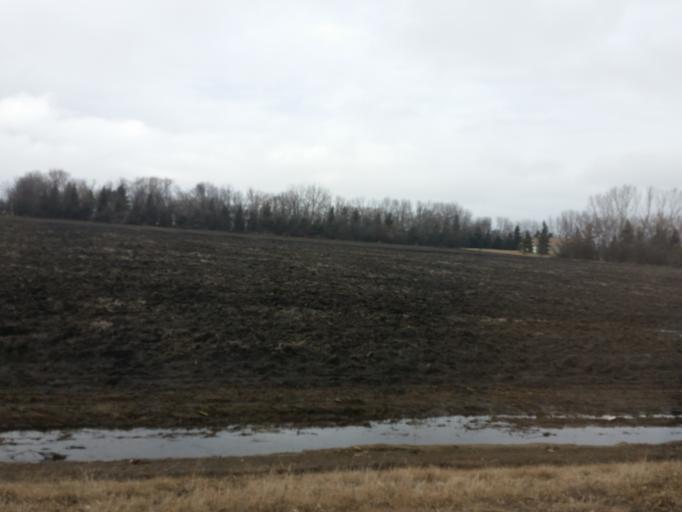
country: US
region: North Dakota
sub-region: Walsh County
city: Grafton
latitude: 48.4272
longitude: -97.3212
